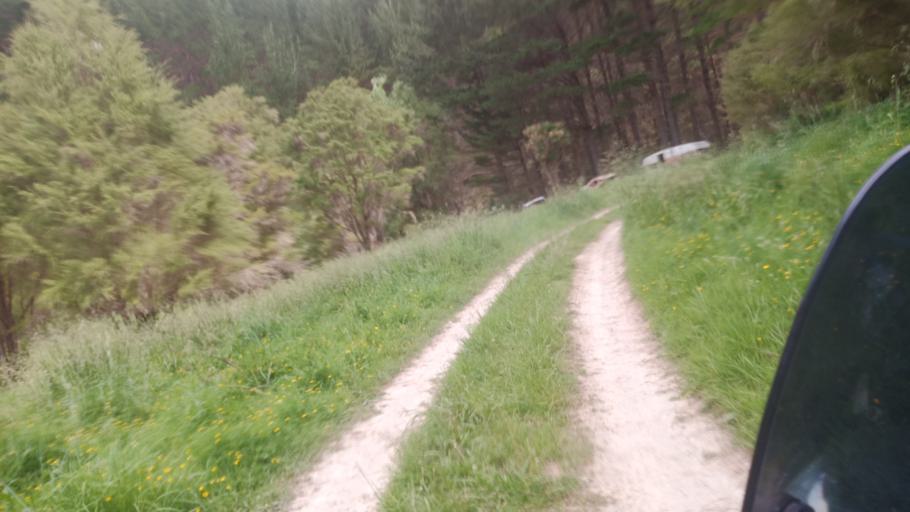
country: NZ
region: Gisborne
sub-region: Gisborne District
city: Gisborne
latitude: -38.4570
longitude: 177.9124
